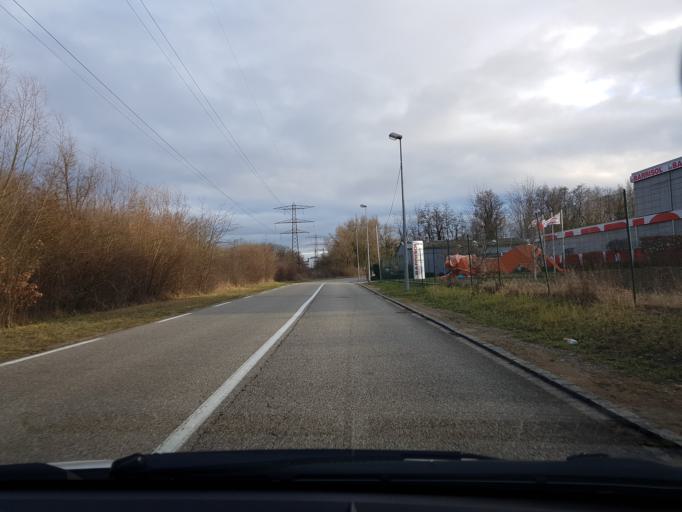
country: FR
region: Alsace
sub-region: Departement du Haut-Rhin
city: Kembs
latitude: 47.6633
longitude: 7.5121
